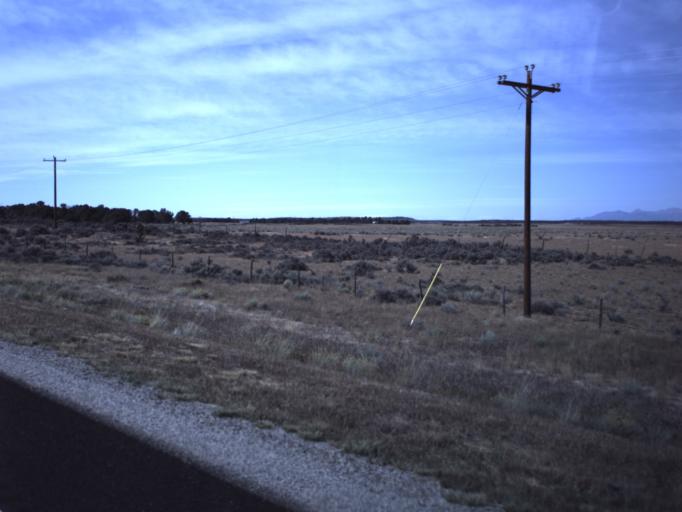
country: US
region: Colorado
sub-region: Dolores County
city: Dove Creek
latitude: 37.8210
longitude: -109.0575
